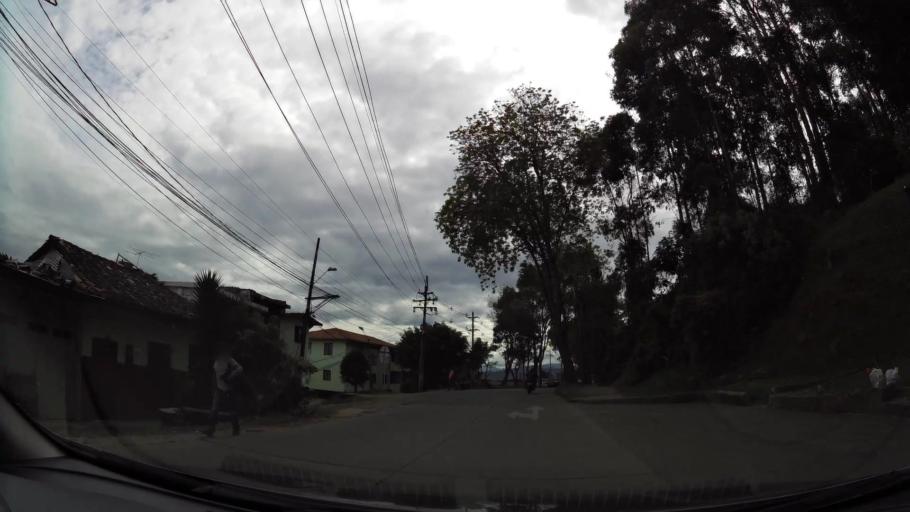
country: CO
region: Antioquia
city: Rionegro
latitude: 6.1521
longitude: -75.3793
